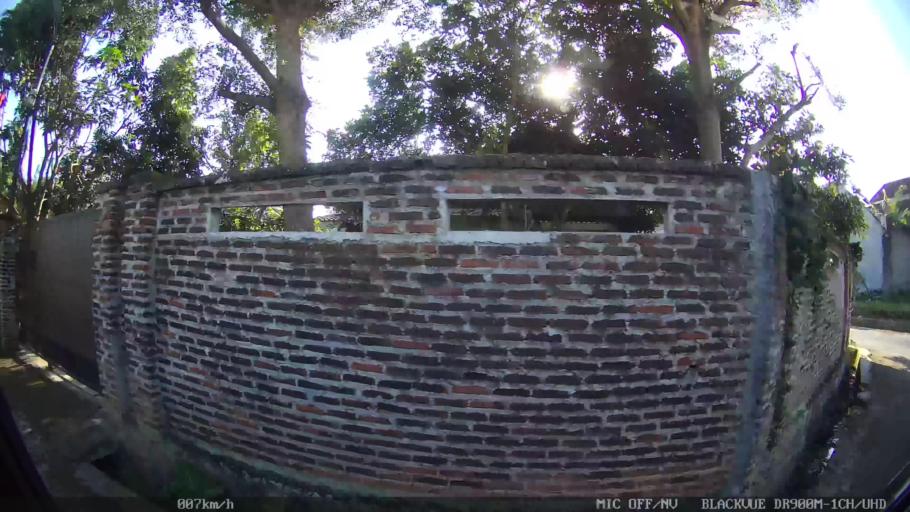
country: ID
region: Lampung
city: Kedaton
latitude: -5.3701
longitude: 105.2308
